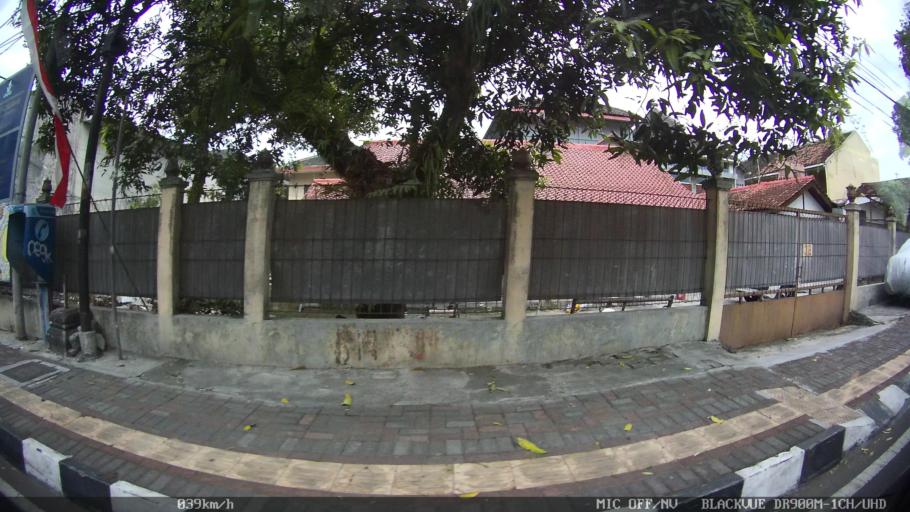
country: ID
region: Daerah Istimewa Yogyakarta
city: Yogyakarta
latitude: -7.7922
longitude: 110.3895
